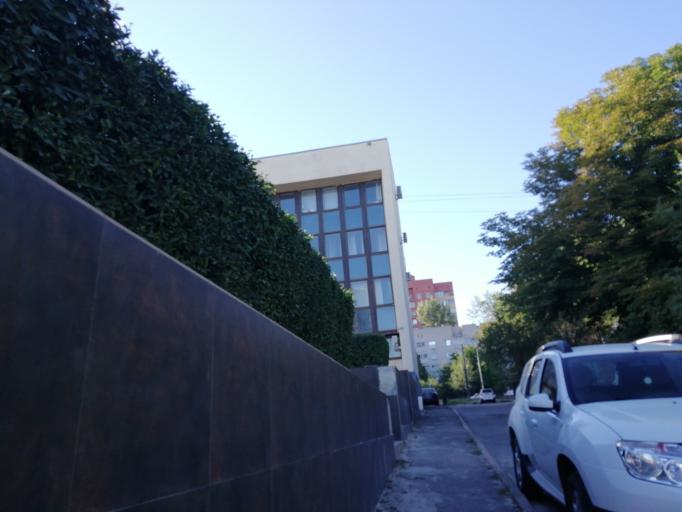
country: RU
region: Rostov
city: Severnyy
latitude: 47.2889
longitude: 39.7105
